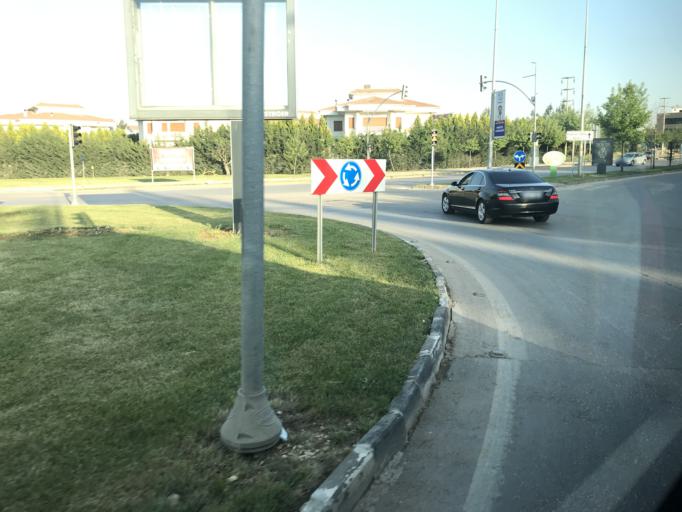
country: TR
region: Gaziantep
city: Sahinbey
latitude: 37.0626
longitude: 37.3205
